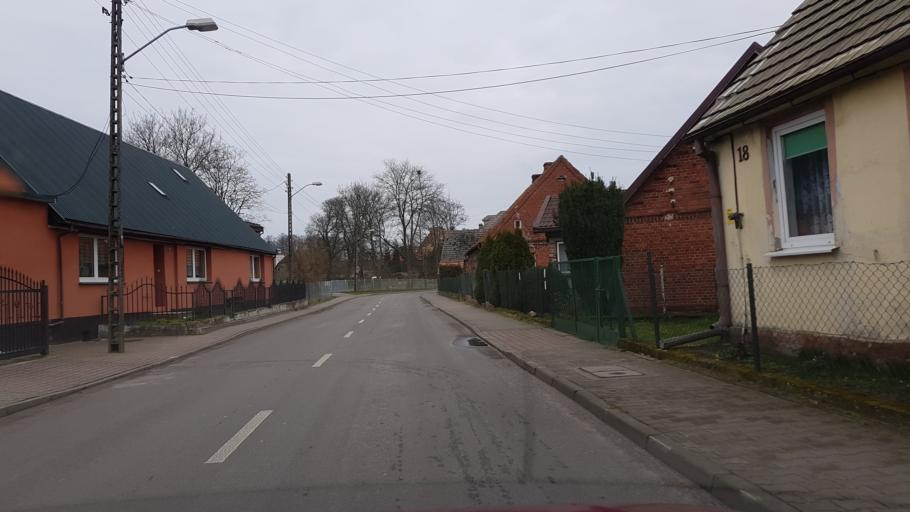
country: PL
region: West Pomeranian Voivodeship
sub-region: Powiat goleniowski
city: Stepnica
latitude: 53.6569
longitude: 14.5120
